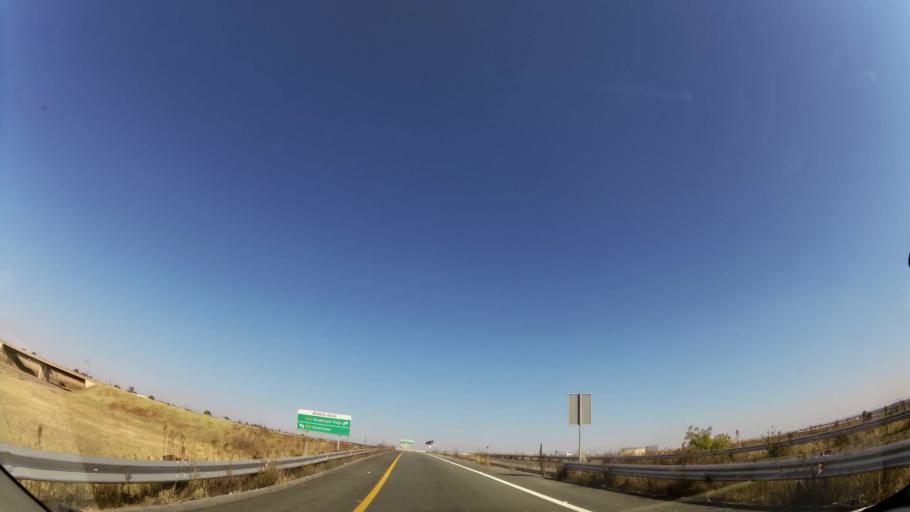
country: ZA
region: Gauteng
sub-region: City of Tshwane Metropolitan Municipality
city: Centurion
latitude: -25.8206
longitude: 28.1809
